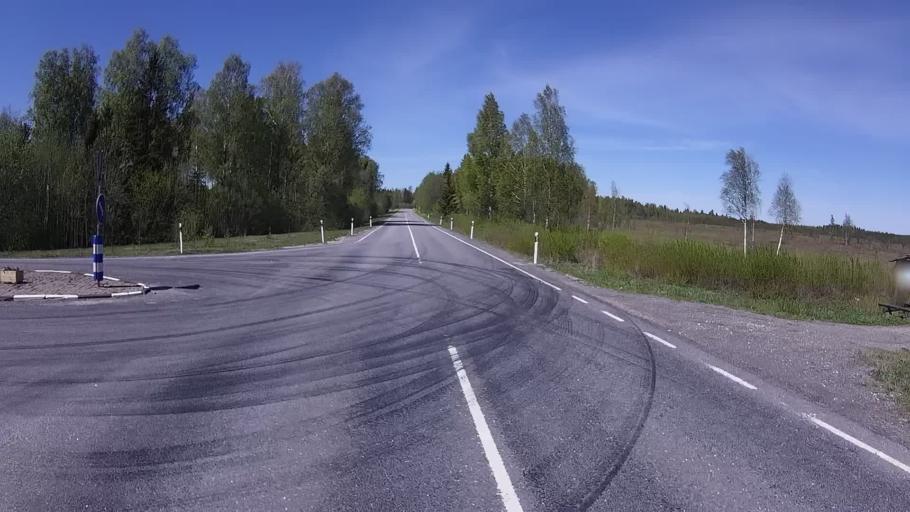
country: EE
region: Raplamaa
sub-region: Kehtna vald
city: Kehtna
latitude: 59.0429
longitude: 25.0311
